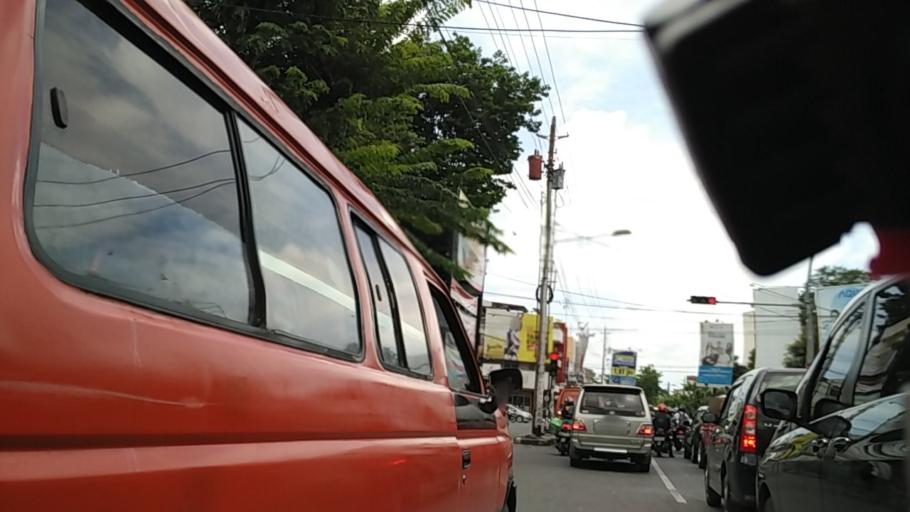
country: ID
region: Central Java
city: Semarang
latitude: -6.9949
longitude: 110.4320
